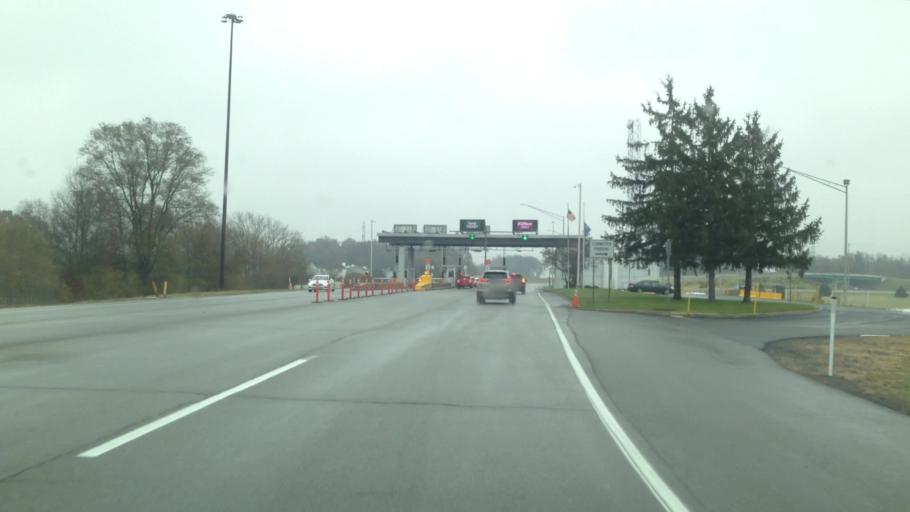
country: US
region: Indiana
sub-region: Saint Joseph County
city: Granger
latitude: 41.7336
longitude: -86.1465
